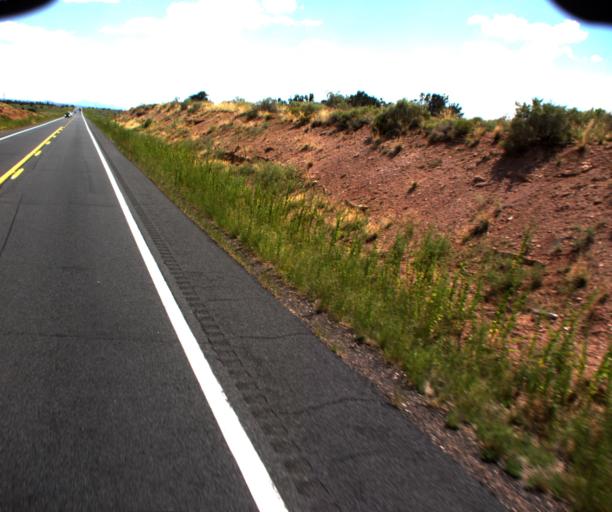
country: US
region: Arizona
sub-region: Coconino County
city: Grand Canyon Village
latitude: 35.7022
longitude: -112.1327
